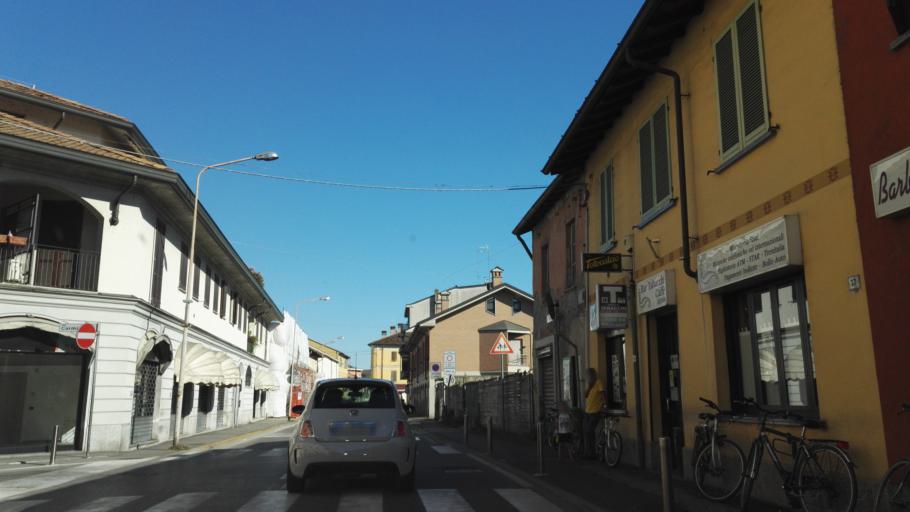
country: IT
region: Lombardy
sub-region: Citta metropolitana di Milano
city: Melegnano
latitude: 45.3619
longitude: 9.3233
